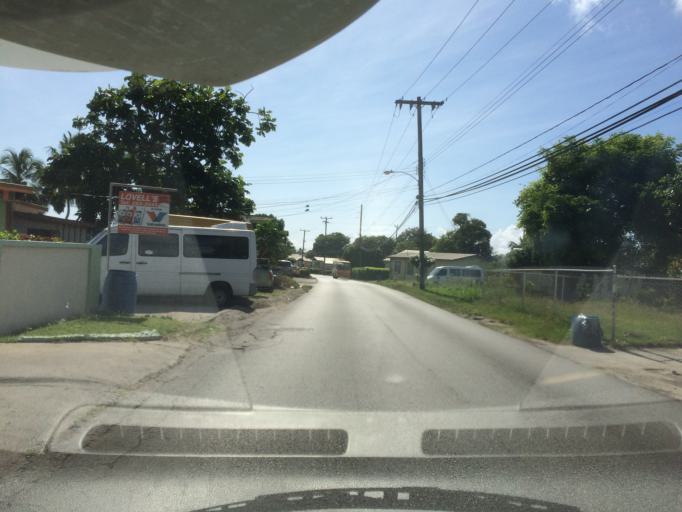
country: BB
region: Christ Church
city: Oistins
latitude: 13.0751
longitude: -59.5374
